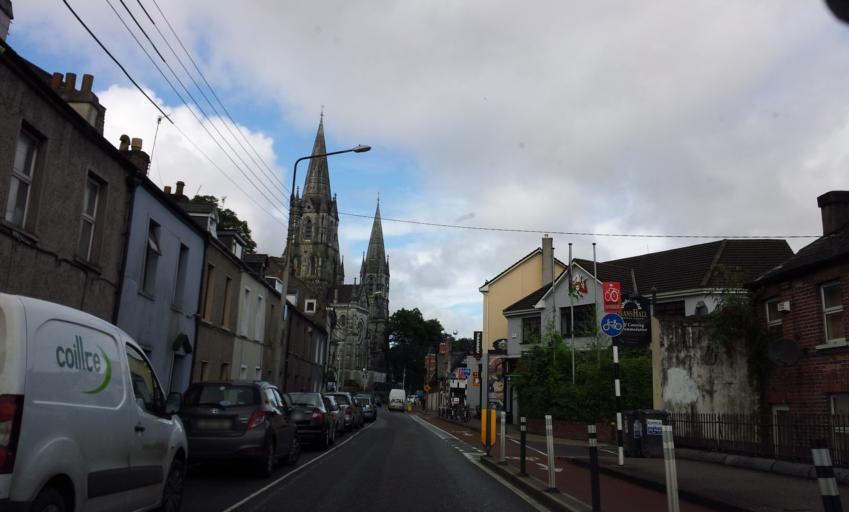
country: IE
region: Munster
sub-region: County Cork
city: Cork
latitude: 51.8951
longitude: -8.4779
